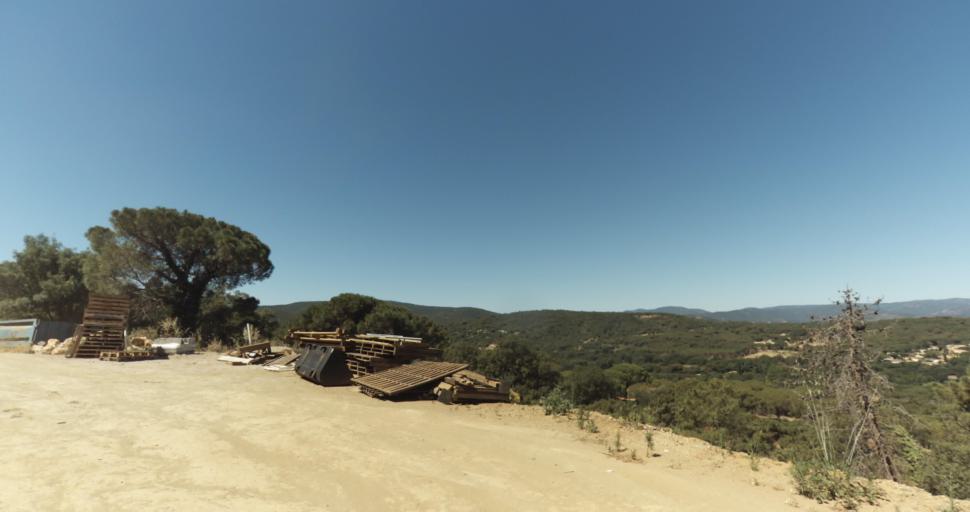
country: FR
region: Provence-Alpes-Cote d'Azur
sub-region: Departement du Var
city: Gassin
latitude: 43.2426
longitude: 6.5794
